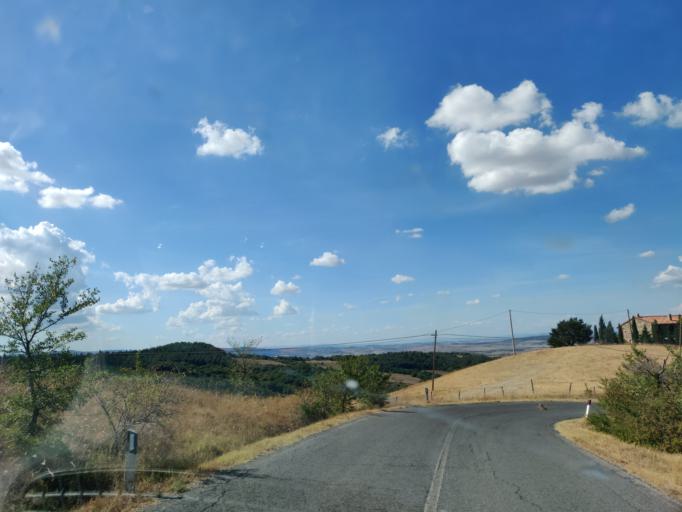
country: IT
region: Tuscany
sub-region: Provincia di Siena
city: Radicofani
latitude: 42.9672
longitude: 11.7335
